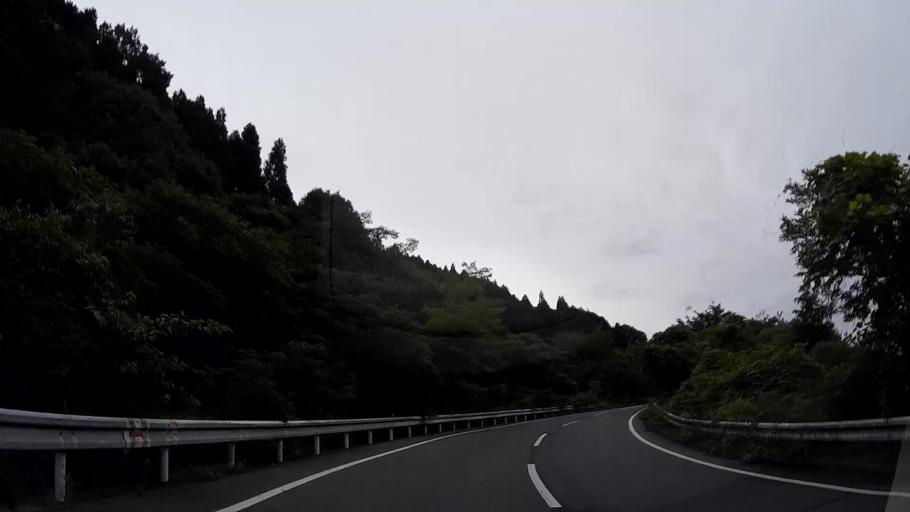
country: JP
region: Kumamoto
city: Kikuchi
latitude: 33.0594
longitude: 130.9041
